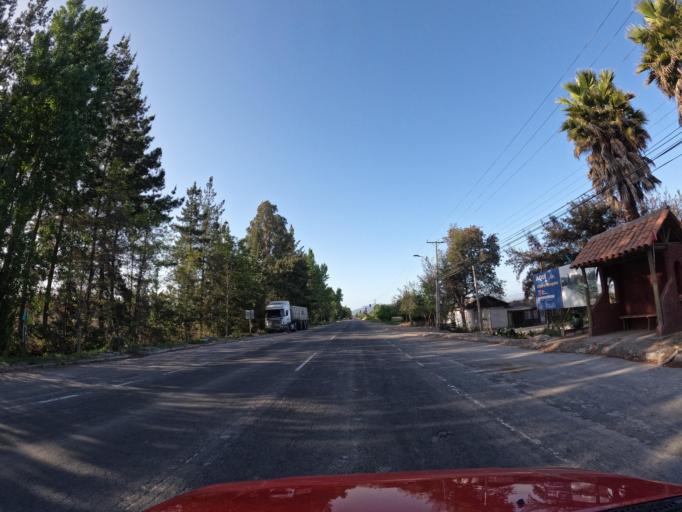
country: CL
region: O'Higgins
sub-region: Provincia de Colchagua
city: Santa Cruz
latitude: -34.4980
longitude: -71.3621
